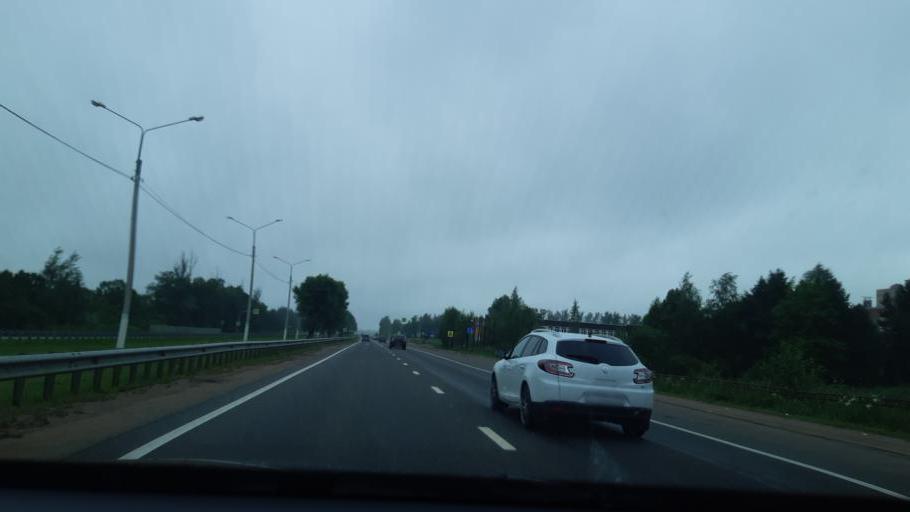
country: RU
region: Smolensk
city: Talashkino
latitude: 54.6838
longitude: 32.1380
